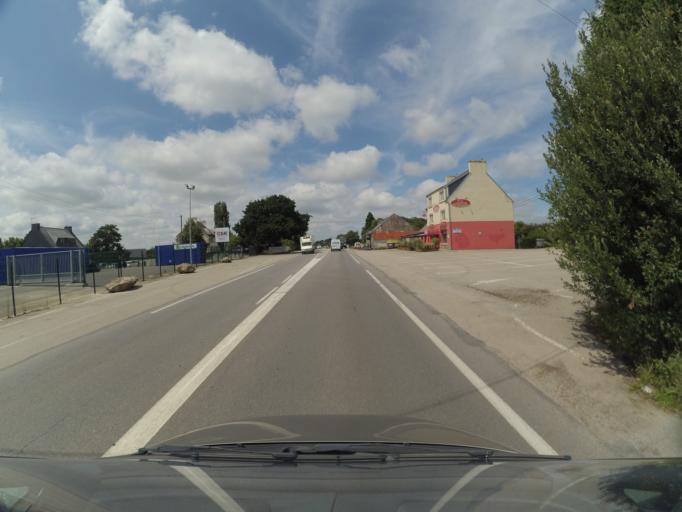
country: FR
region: Brittany
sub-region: Departement du Finistere
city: Ergue-Gaberic
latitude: 47.9773
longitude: -4.0076
